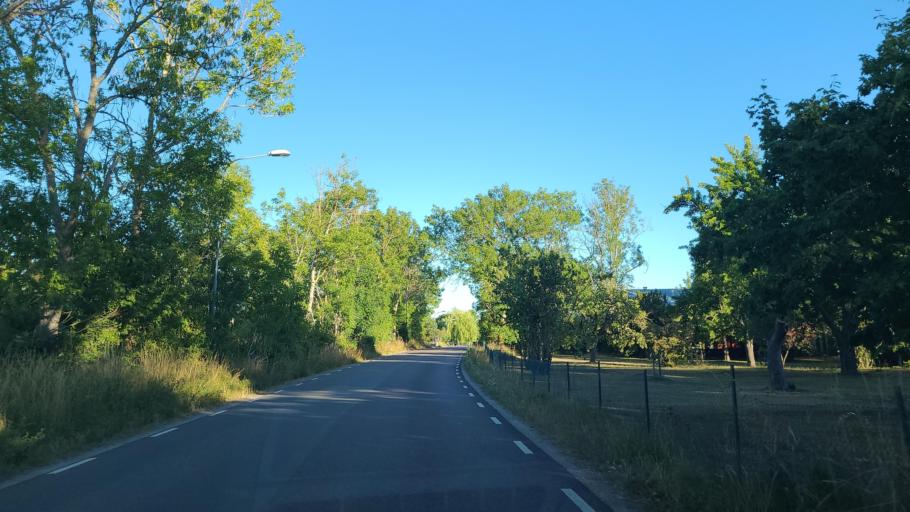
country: SE
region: Kalmar
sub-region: Oskarshamns Kommun
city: Oskarshamn
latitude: 57.3216
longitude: 17.0144
